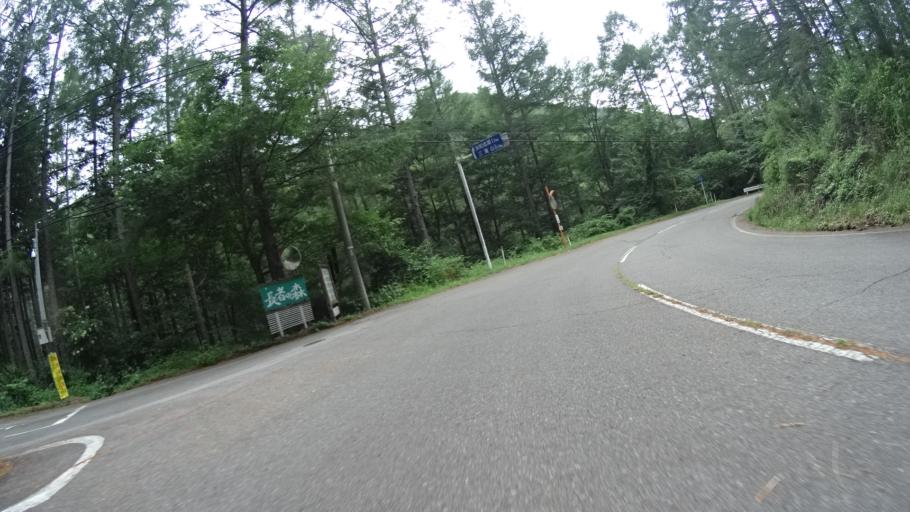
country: JP
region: Nagano
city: Saku
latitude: 36.0685
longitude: 138.6258
